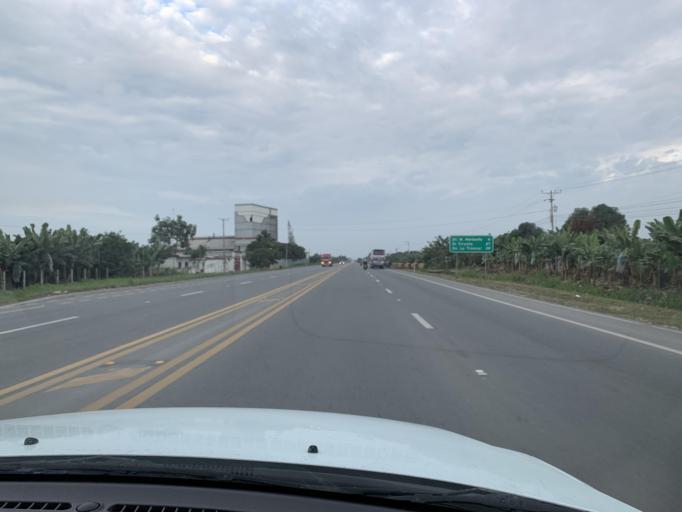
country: EC
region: Guayas
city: Yaguachi Nuevo
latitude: -2.2547
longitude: -79.6177
